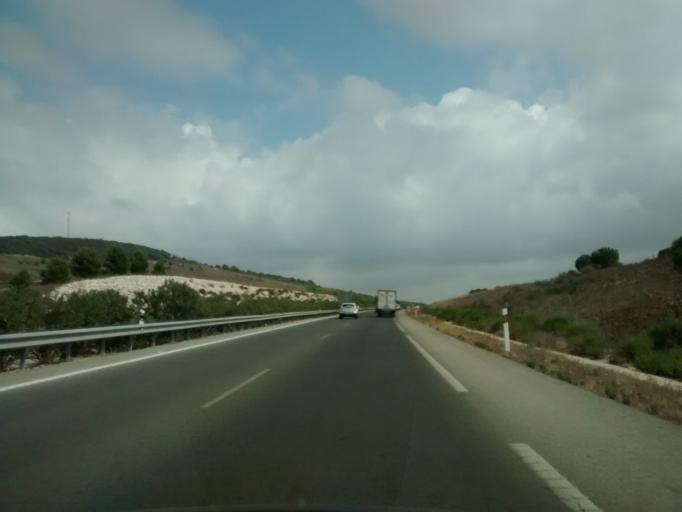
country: ES
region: Andalusia
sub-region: Provincia de Cadiz
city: Conil de la Frontera
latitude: 36.3197
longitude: -6.0569
